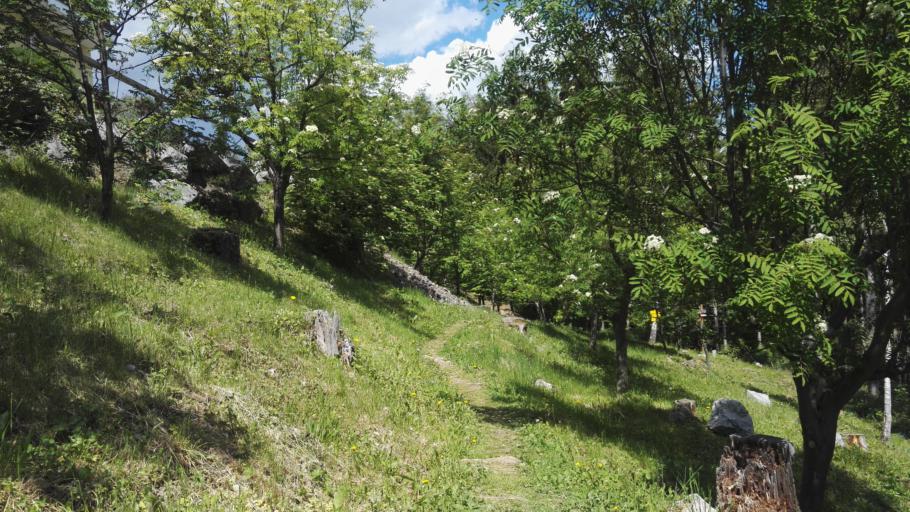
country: AT
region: Styria
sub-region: Graz Stadt
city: Goesting
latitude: 47.0905
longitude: 15.3857
